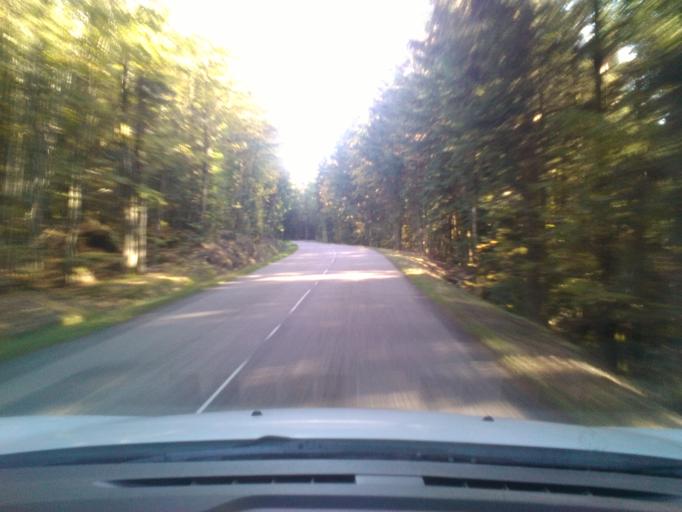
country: FR
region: Lorraine
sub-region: Departement des Vosges
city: Etival-Clairefontaine
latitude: 48.2920
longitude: 6.7848
